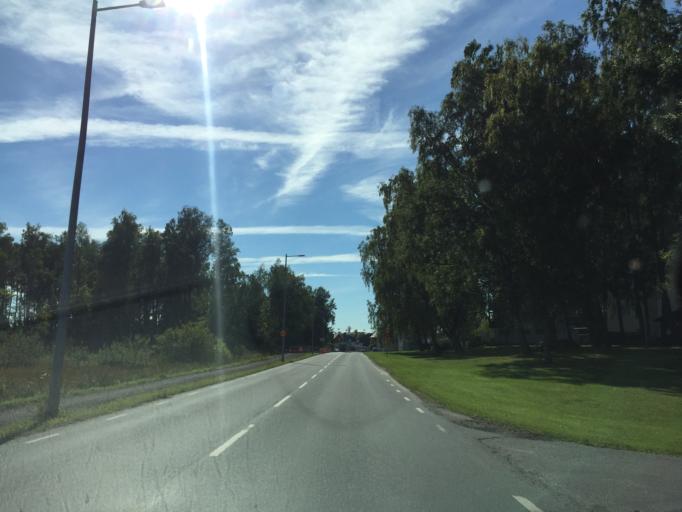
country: SE
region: OErebro
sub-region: Orebro Kommun
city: Orebro
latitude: 59.2865
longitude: 15.2382
